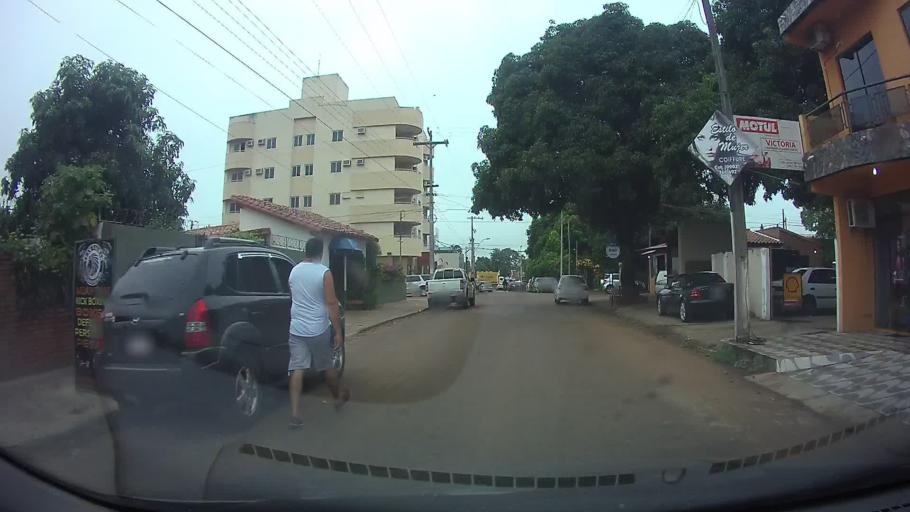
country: PY
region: Central
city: Itaugua
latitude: -25.3918
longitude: -57.3532
